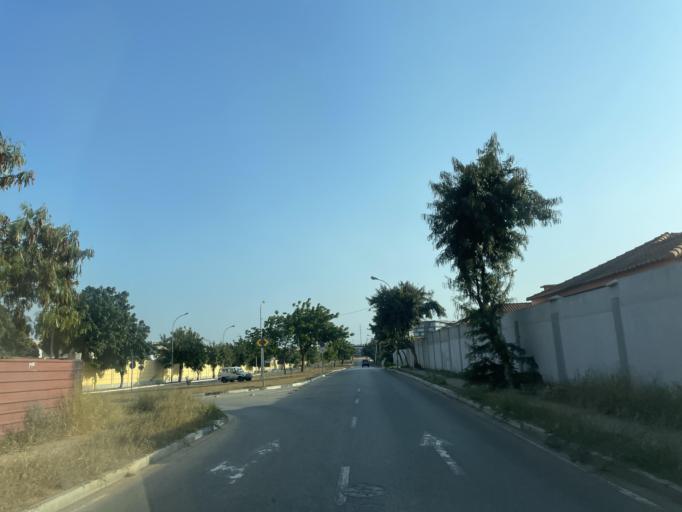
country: AO
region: Luanda
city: Luanda
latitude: -8.9148
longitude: 13.1808
